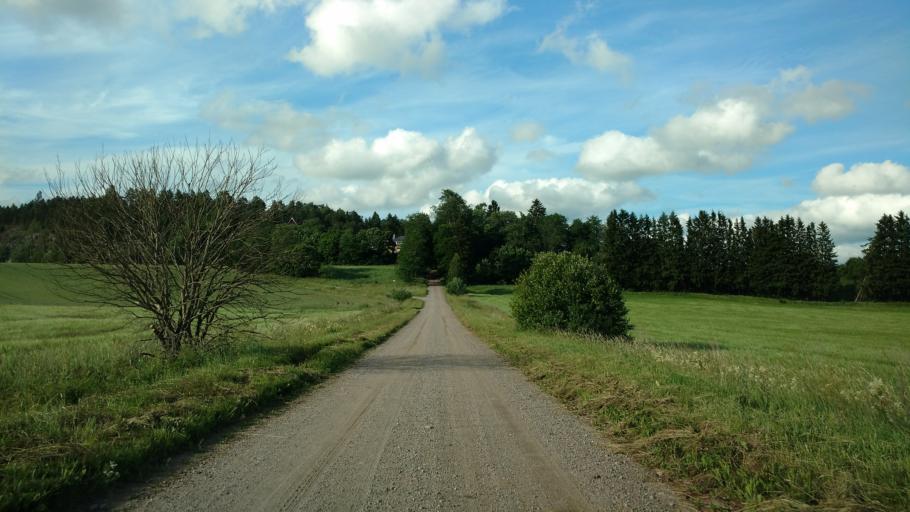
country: FI
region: Varsinais-Suomi
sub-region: Salo
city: Salo
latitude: 60.4227
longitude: 23.1754
